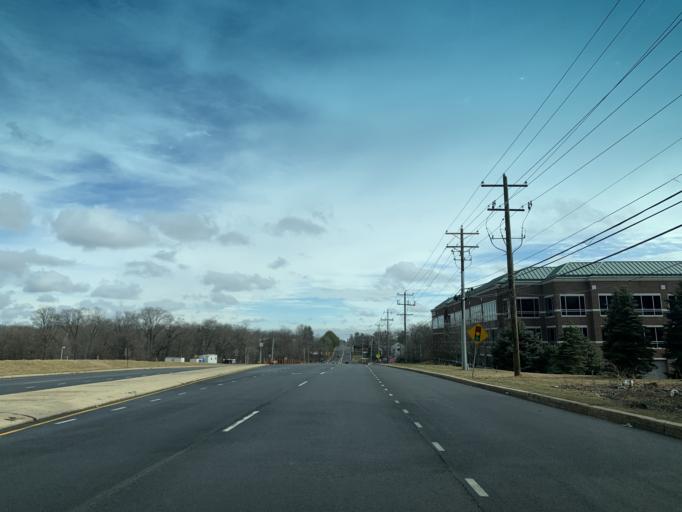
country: US
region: Delaware
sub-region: New Castle County
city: Elsmere
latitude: 39.7582
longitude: -75.6027
